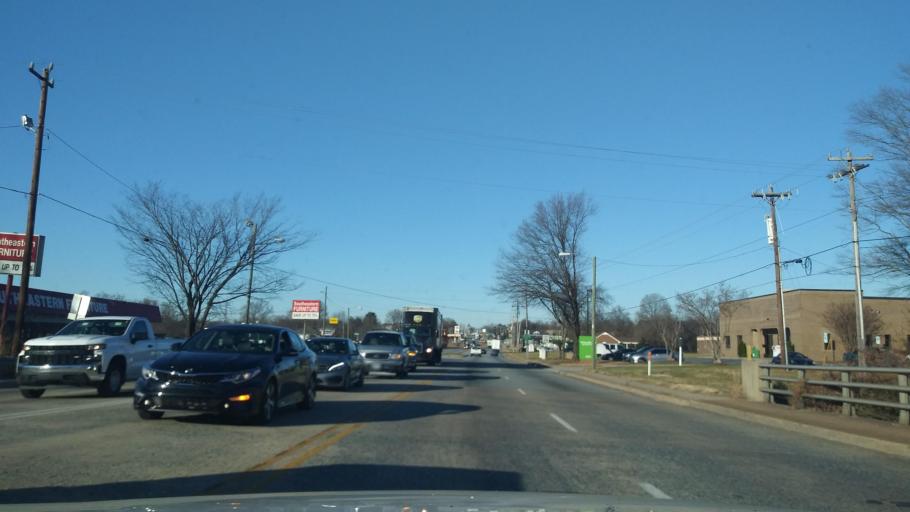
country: US
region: North Carolina
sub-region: Guilford County
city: Greensboro
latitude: 36.0297
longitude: -79.7916
